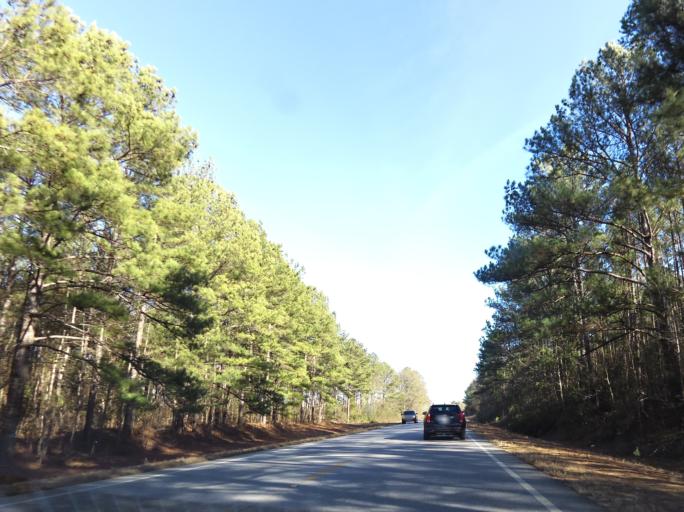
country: US
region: Georgia
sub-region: Crawford County
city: Roberta
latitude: 32.7225
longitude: -84.0281
